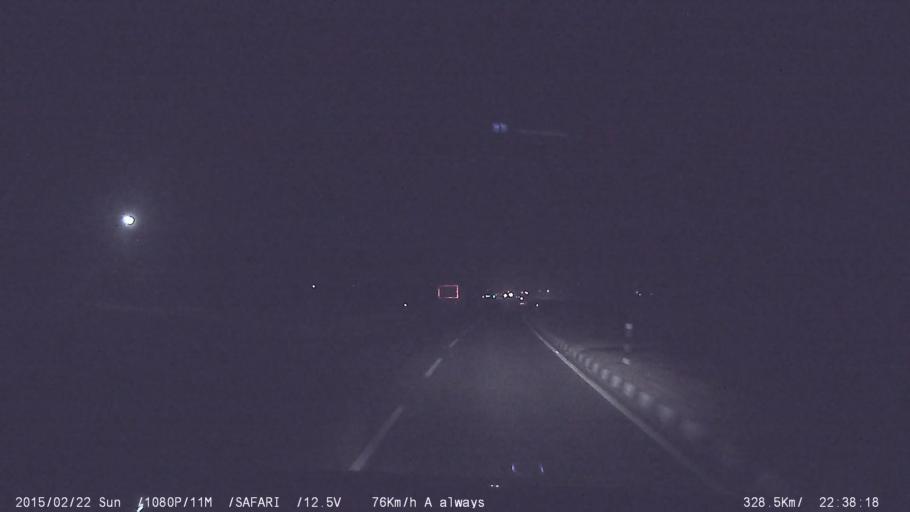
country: IN
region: Tamil Nadu
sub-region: Namakkal
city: Velur
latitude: 11.1674
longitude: 78.0318
